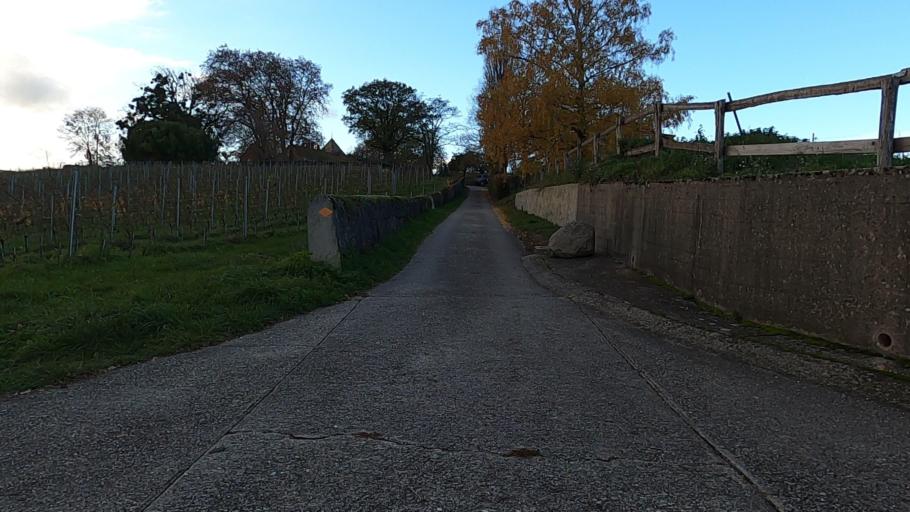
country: CH
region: Vaud
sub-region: Morges District
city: Morges
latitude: 46.5172
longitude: 6.4621
